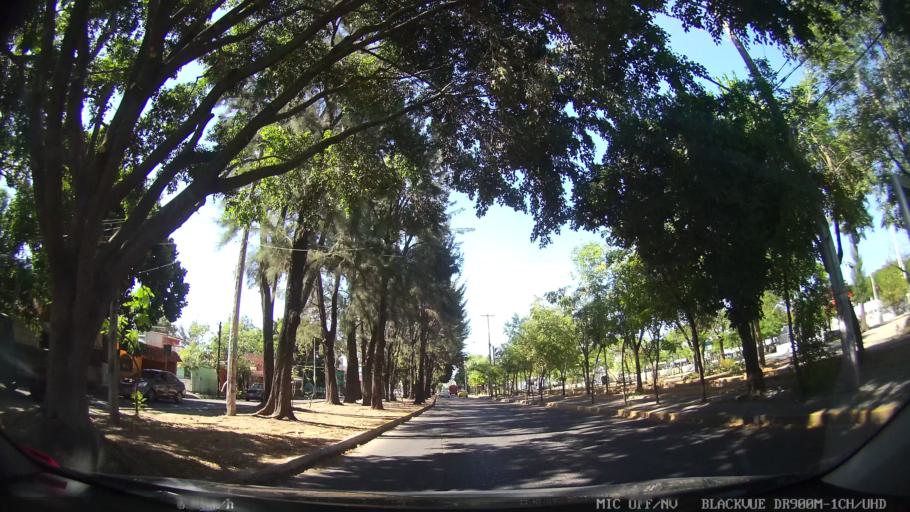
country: MX
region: Jalisco
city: Tlaquepaque
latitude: 20.6613
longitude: -103.2985
